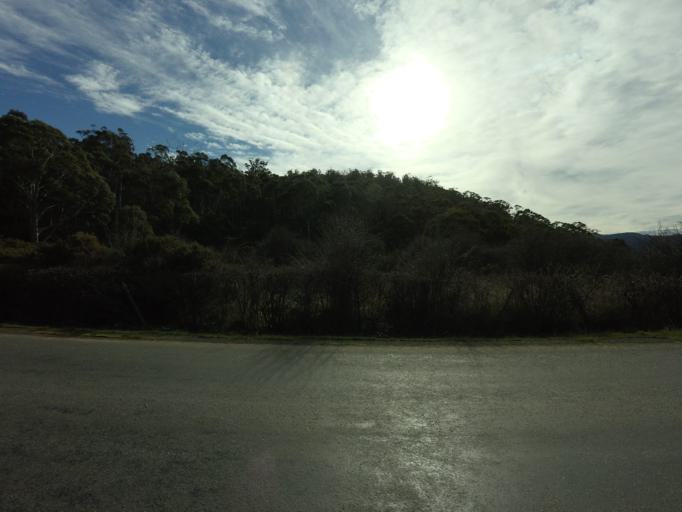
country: AU
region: Tasmania
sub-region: Derwent Valley
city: New Norfolk
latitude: -42.7812
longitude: 147.0059
